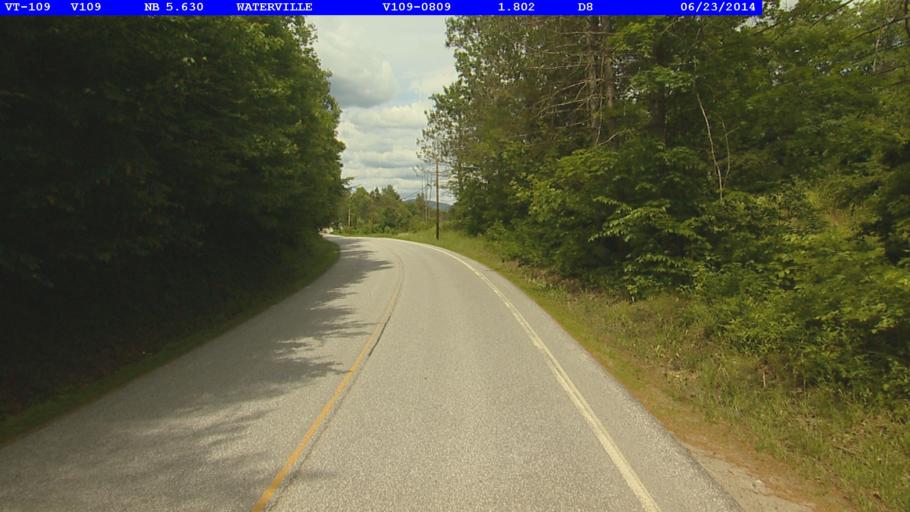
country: US
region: Vermont
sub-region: Lamoille County
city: Johnson
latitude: 44.7060
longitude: -72.7605
